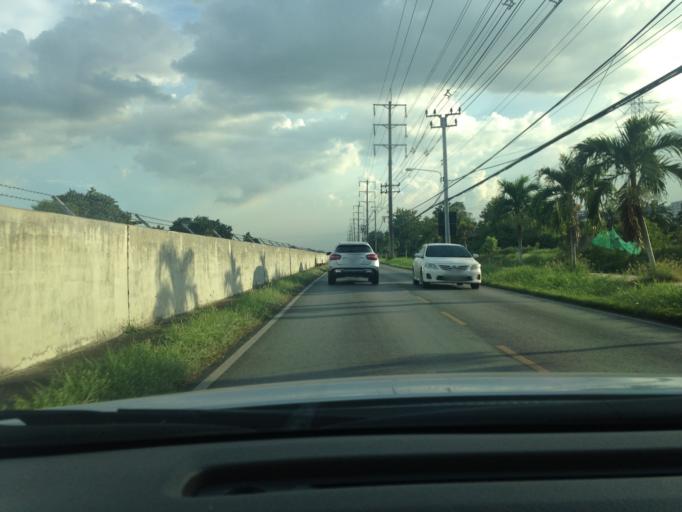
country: TH
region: Bangkok
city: Don Mueang
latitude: 13.9215
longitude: 100.5605
